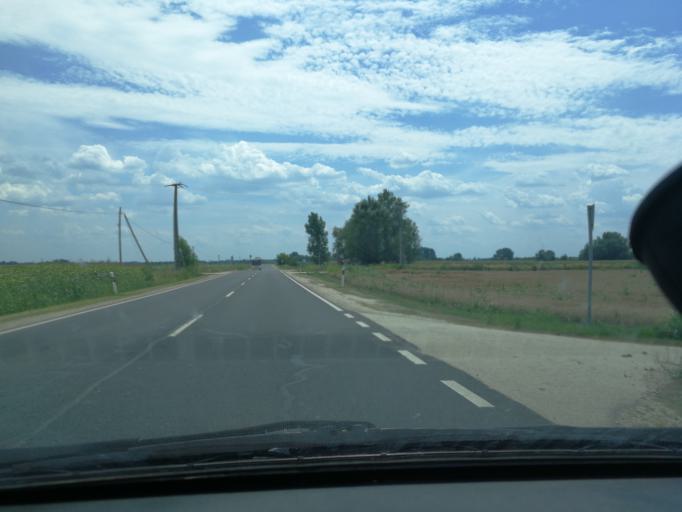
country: HU
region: Bacs-Kiskun
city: Kalocsa
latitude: 46.5647
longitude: 18.9762
